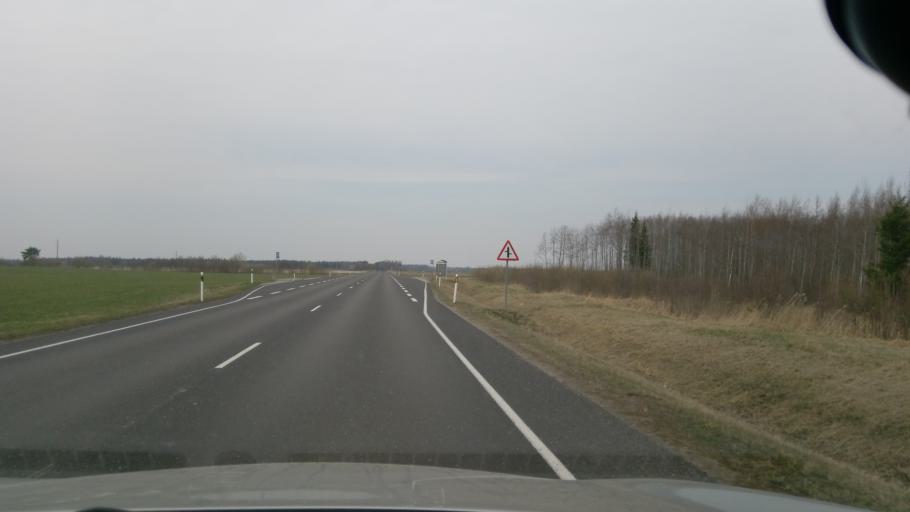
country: EE
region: Viljandimaa
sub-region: Vohma linn
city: Vohma
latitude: 58.7265
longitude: 25.5992
